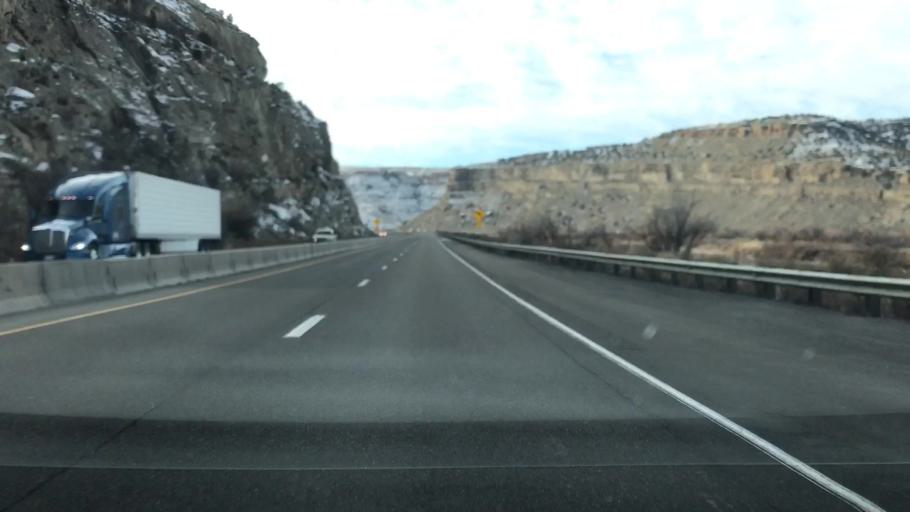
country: US
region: Colorado
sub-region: Mesa County
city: Palisade
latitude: 39.2637
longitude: -108.2563
